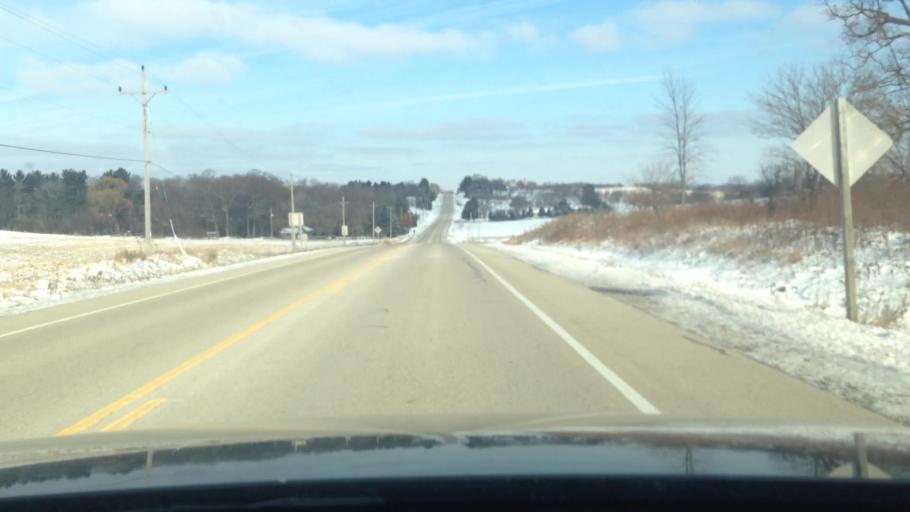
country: US
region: Wisconsin
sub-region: Walworth County
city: East Troy
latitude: 42.7478
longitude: -88.4061
